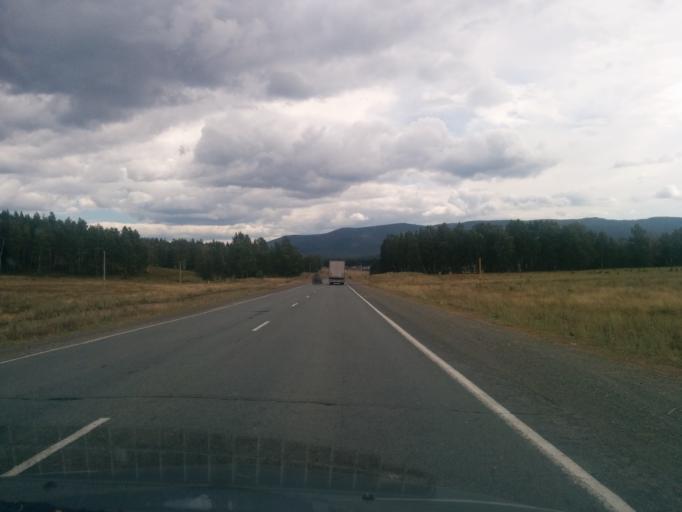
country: RU
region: Bashkortostan
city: Lomovka
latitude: 53.8899
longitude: 58.0958
